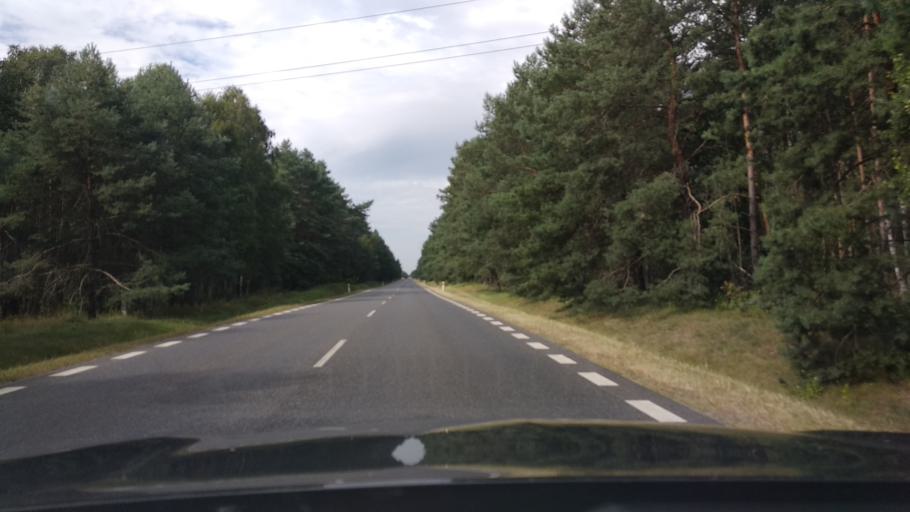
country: PL
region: Masovian Voivodeship
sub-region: Powiat legionowski
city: Serock
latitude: 52.5390
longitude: 21.1191
